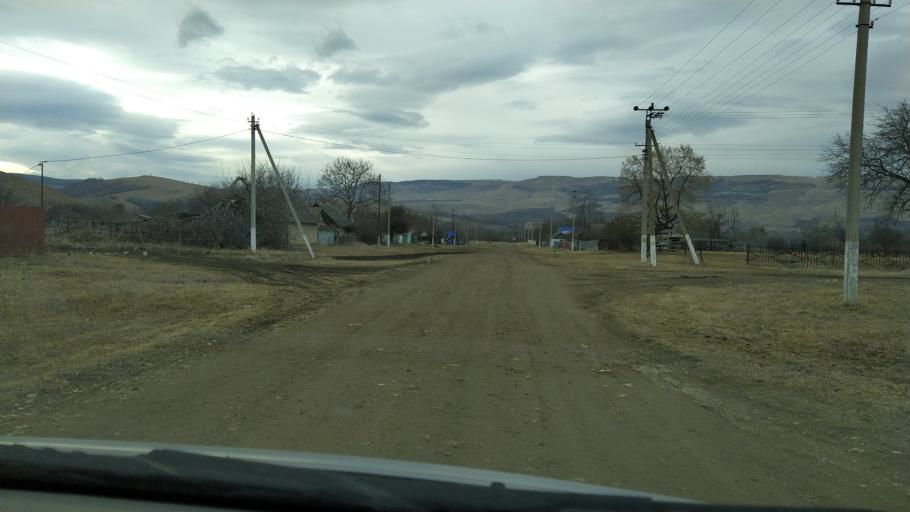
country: RU
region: Krasnodarskiy
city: Peredovaya
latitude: 44.0827
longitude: 41.3682
